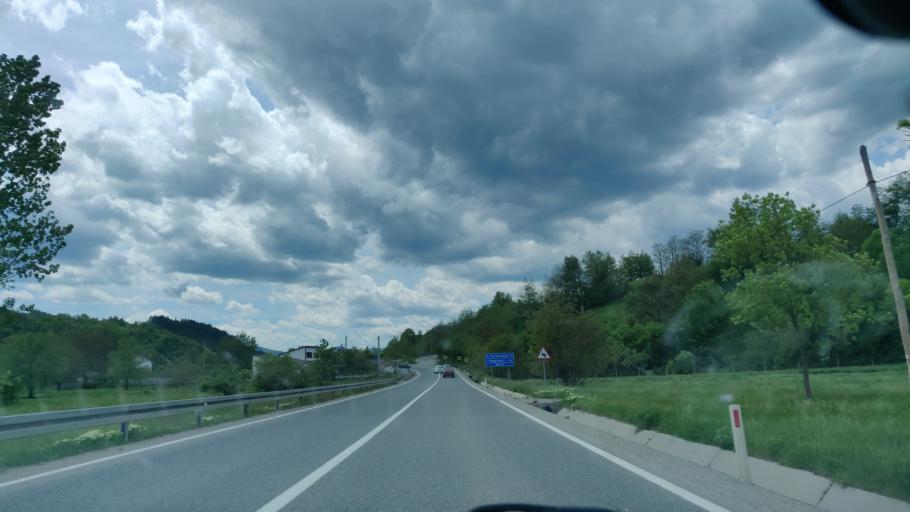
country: RO
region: Vrancea
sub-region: Comuna Negrilesti
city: Negrilesti
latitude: 45.9230
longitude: 26.7080
